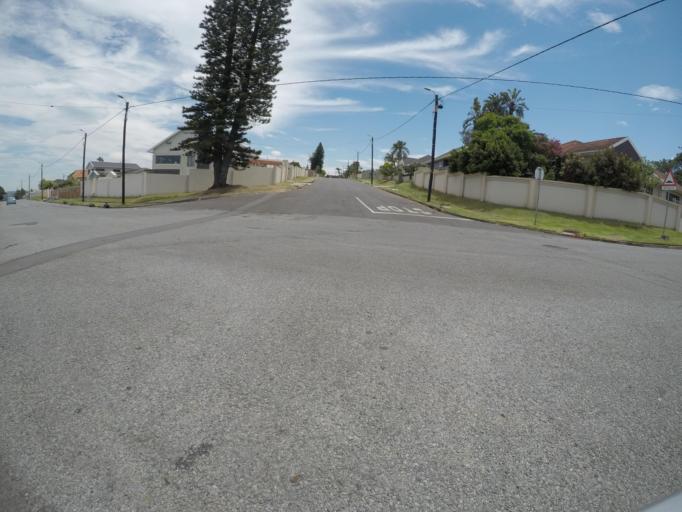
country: ZA
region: Eastern Cape
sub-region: Buffalo City Metropolitan Municipality
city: East London
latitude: -33.0389
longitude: 27.8547
